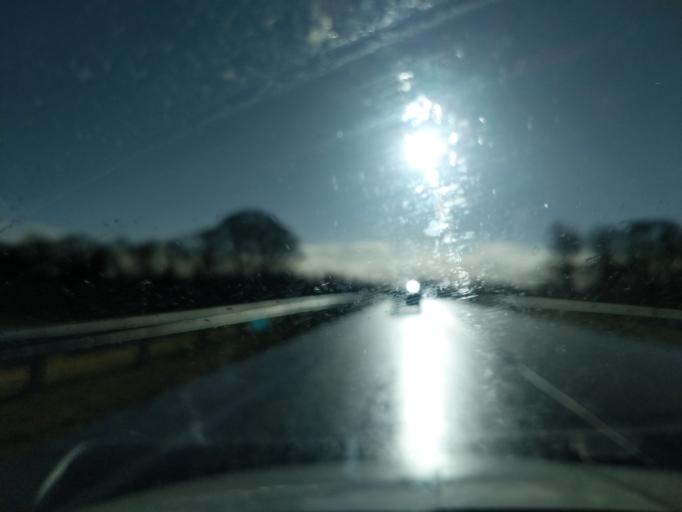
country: GB
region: England
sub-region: North Yorkshire
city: Bedale
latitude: 54.2961
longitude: -1.5916
